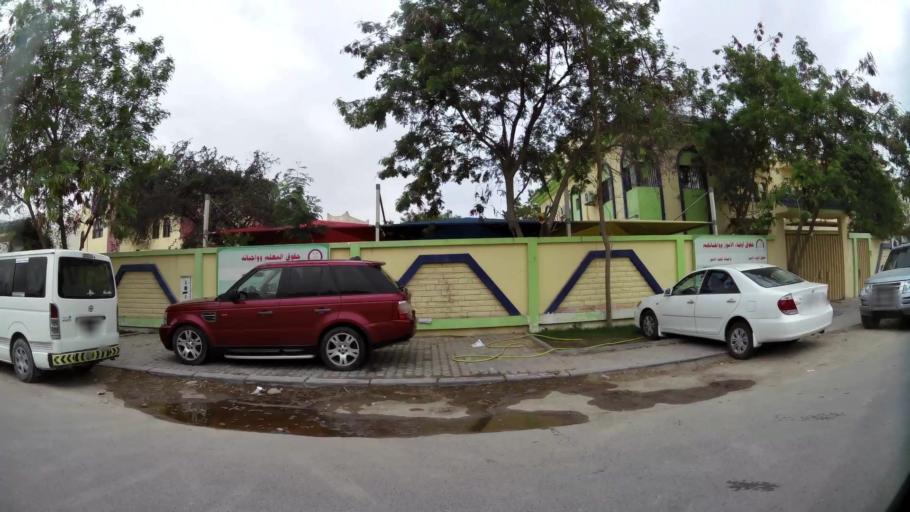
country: QA
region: Baladiyat ar Rayyan
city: Ar Rayyan
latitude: 25.2495
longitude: 51.4386
